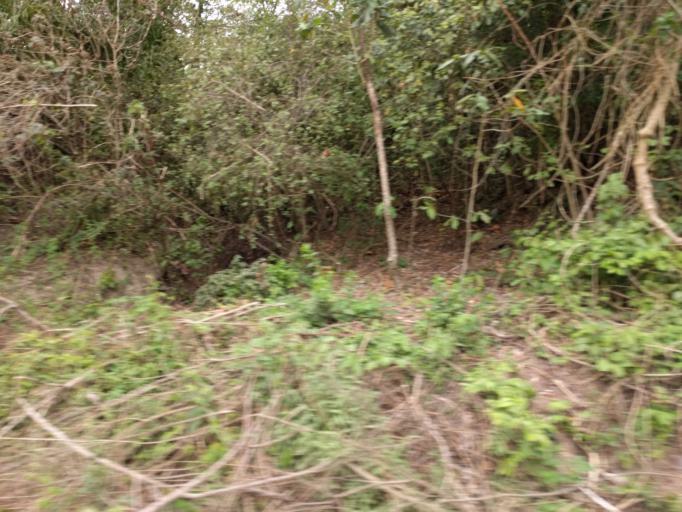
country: BO
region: Santa Cruz
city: Santiago del Torno
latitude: -17.9172
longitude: -63.4263
